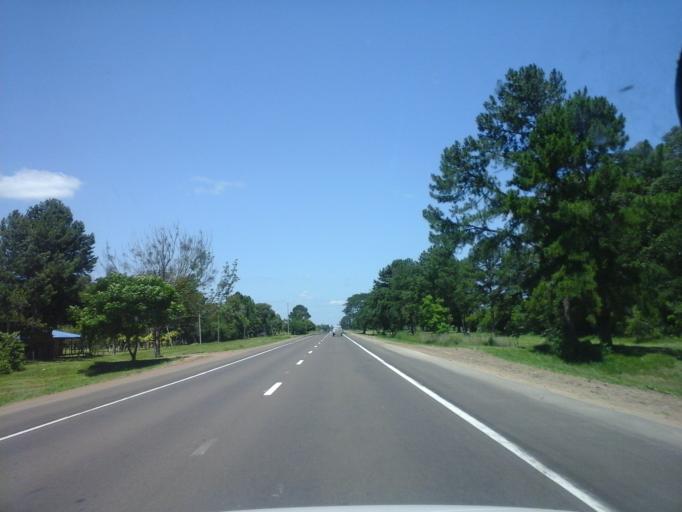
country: AR
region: Corrientes
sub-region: Departamento de San Cosme
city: San Cosme
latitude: -27.3672
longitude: -58.3614
